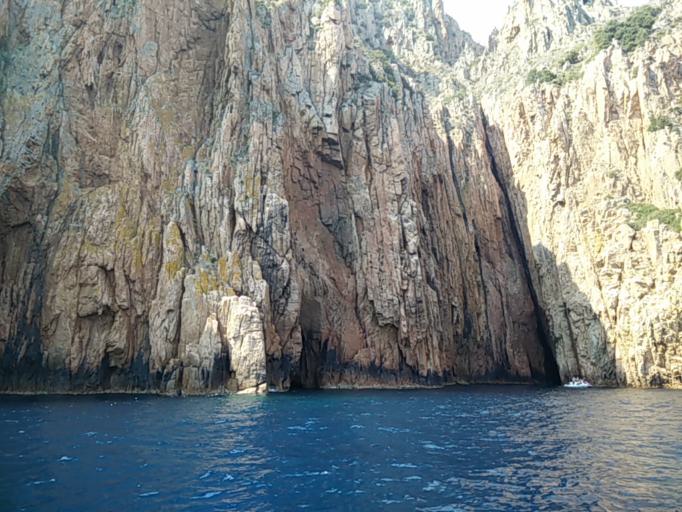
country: FR
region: Corsica
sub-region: Departement de la Corse-du-Sud
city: Cargese
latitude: 42.2395
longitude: 8.5515
